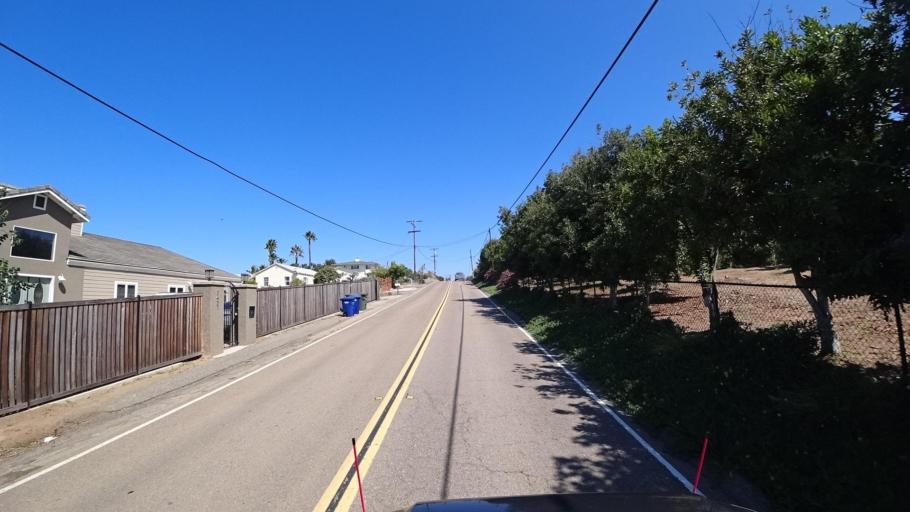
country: US
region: California
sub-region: San Diego County
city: Bonsall
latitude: 33.3299
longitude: -117.2216
